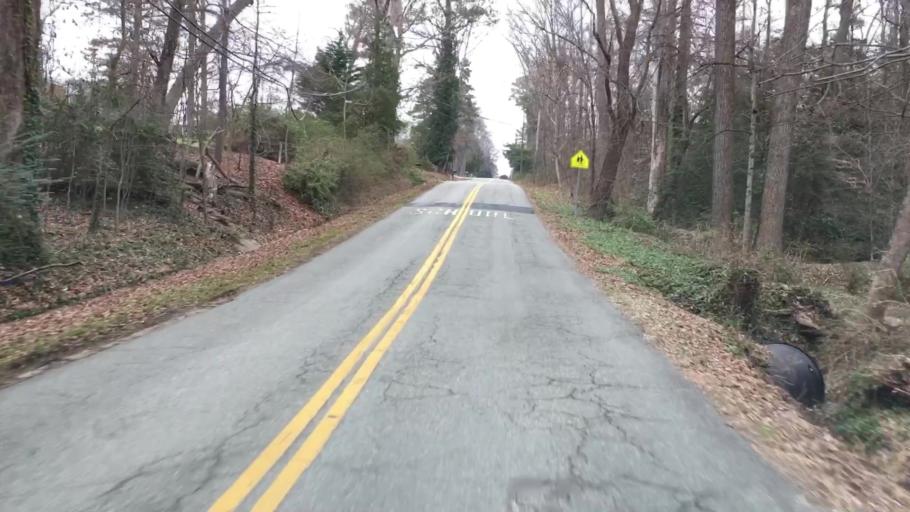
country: US
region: Virginia
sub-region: Chesterfield County
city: Bon Air
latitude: 37.5276
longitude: -77.5603
